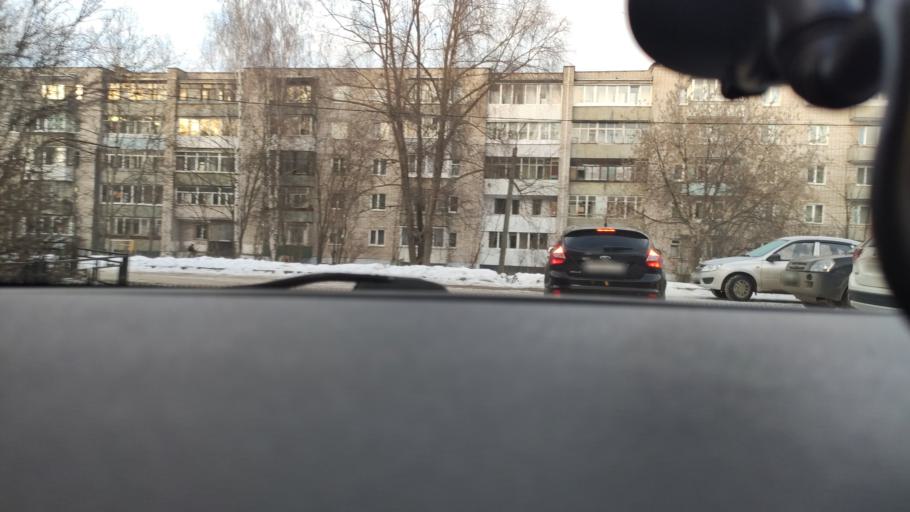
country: RU
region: Perm
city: Perm
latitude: 58.1122
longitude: 56.2816
